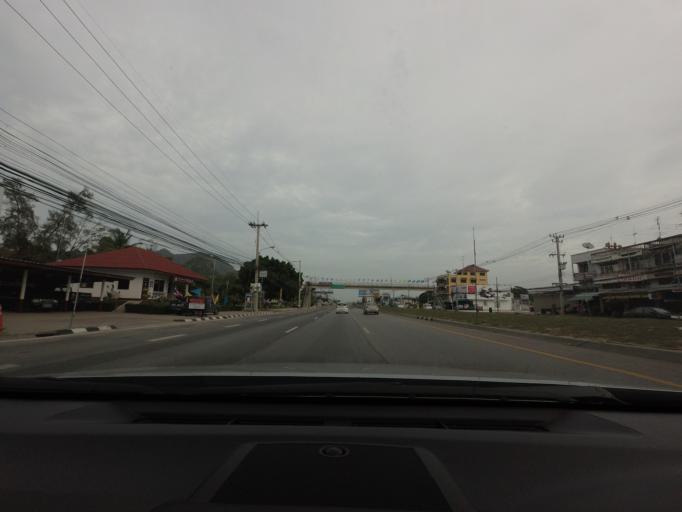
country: TH
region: Phetchaburi
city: Cha-am
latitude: 12.8403
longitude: 99.9306
